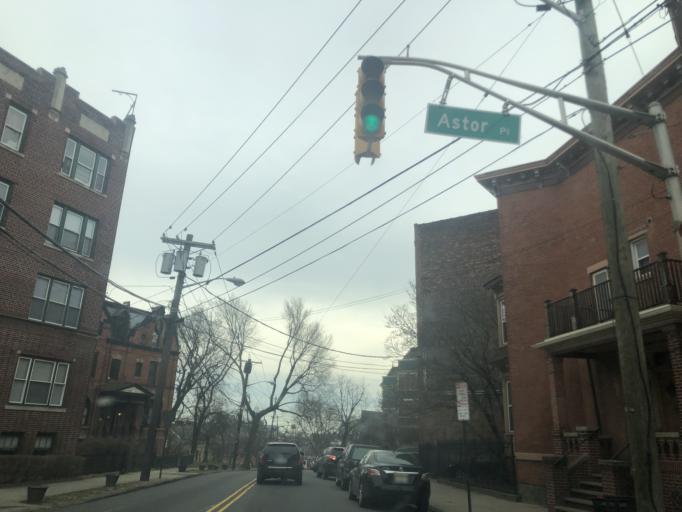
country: US
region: New Jersey
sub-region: Hudson County
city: Jersey City
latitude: 40.7179
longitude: -74.0675
